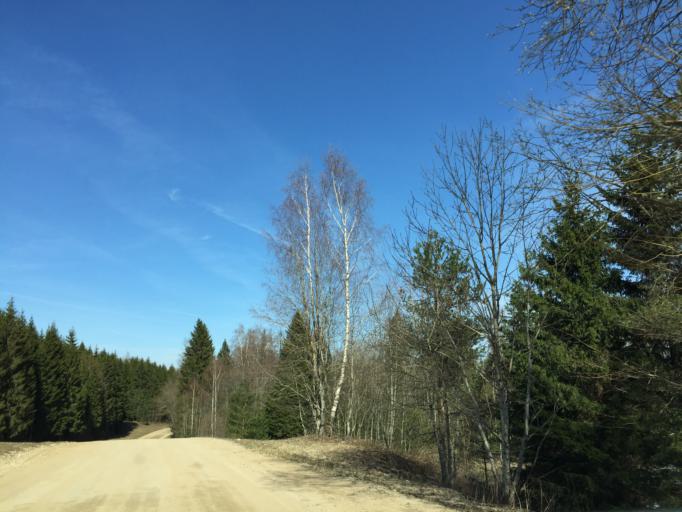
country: EE
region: Vorumaa
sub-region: Antsla vald
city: Vana-Antsla
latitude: 57.9892
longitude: 26.3689
